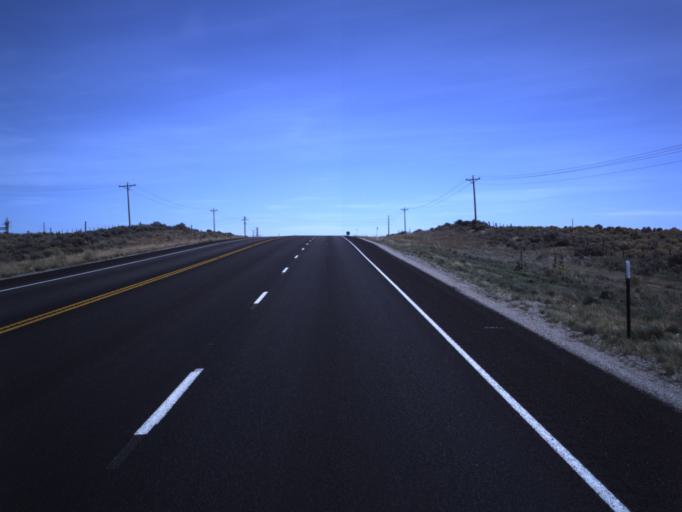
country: US
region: Utah
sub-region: San Juan County
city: Monticello
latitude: 37.8721
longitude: -109.2605
